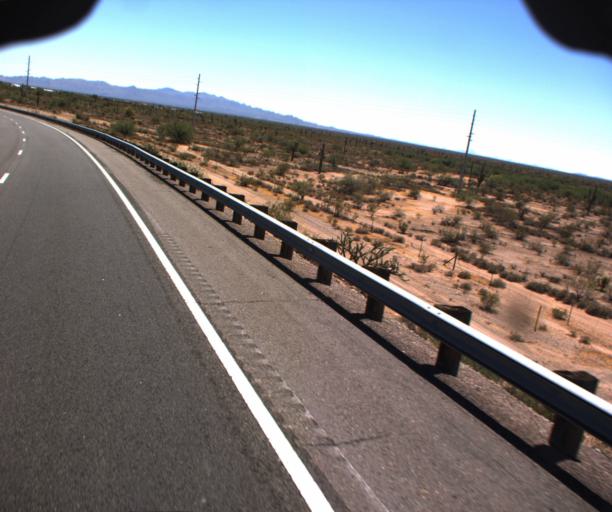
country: US
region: Arizona
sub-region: Maricopa County
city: Wickenburg
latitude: 33.8423
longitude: -112.6133
